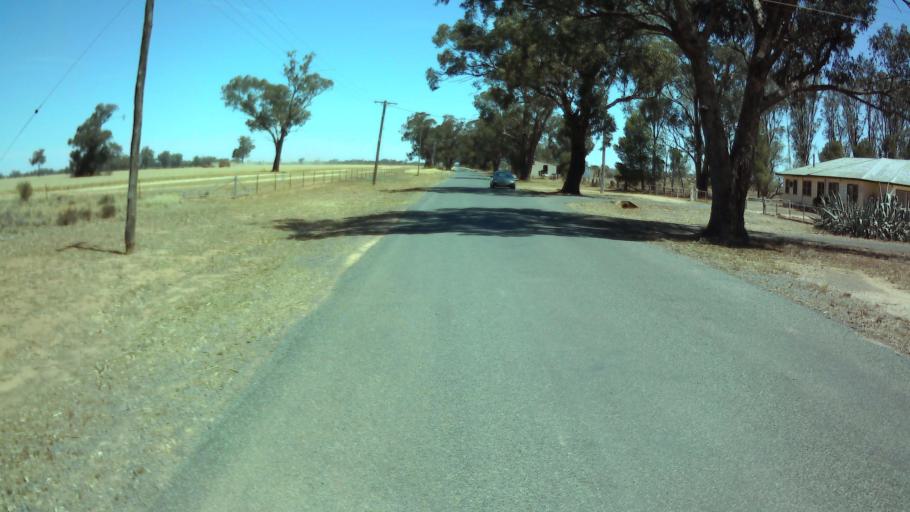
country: AU
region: New South Wales
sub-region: Weddin
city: Grenfell
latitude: -34.0143
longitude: 147.7940
